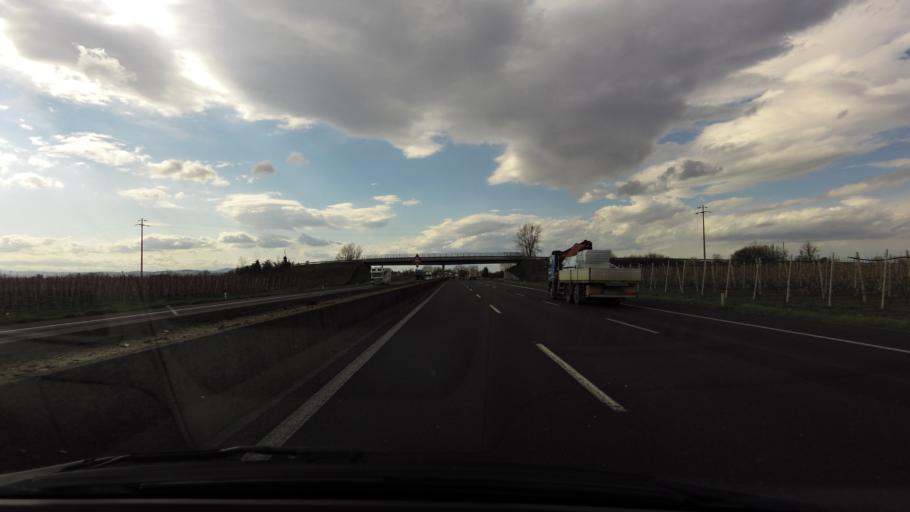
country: IT
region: Emilia-Romagna
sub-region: Provincia di Bologna
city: Mordano
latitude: 44.3601
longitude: 11.7959
